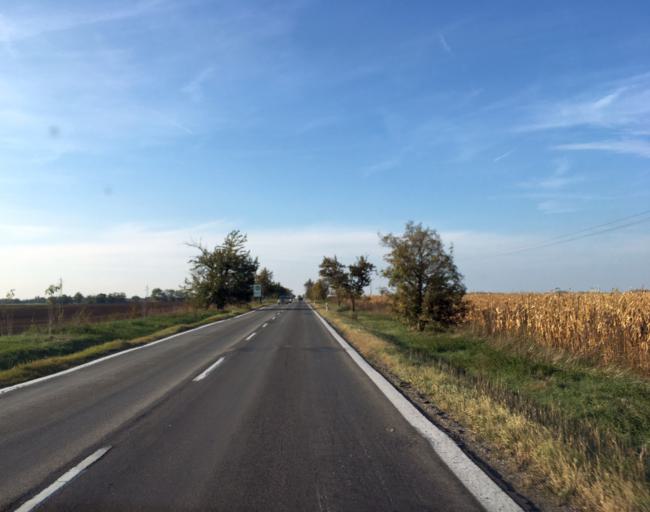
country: SK
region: Nitriansky
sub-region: Okres Nove Zamky
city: Nove Zamky
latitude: 48.0302
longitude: 18.1332
